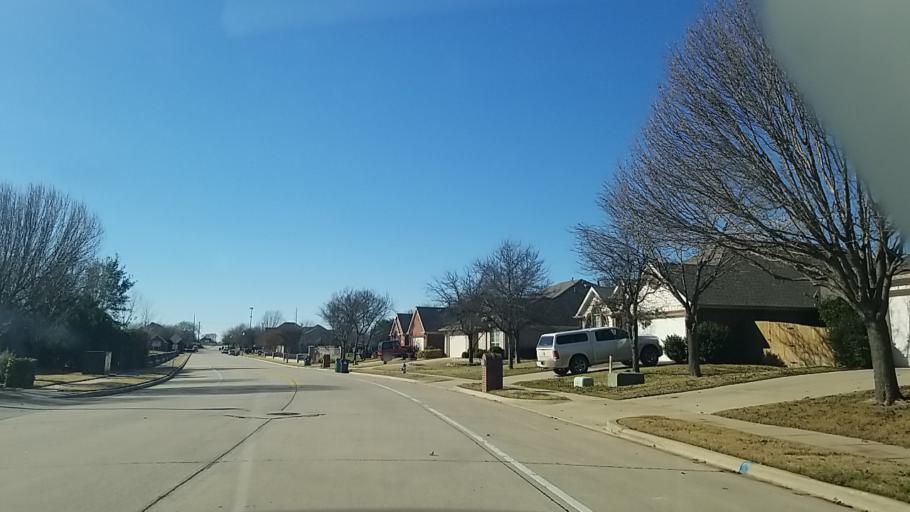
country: US
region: Texas
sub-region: Denton County
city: Corinth
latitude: 33.1515
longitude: -97.0929
